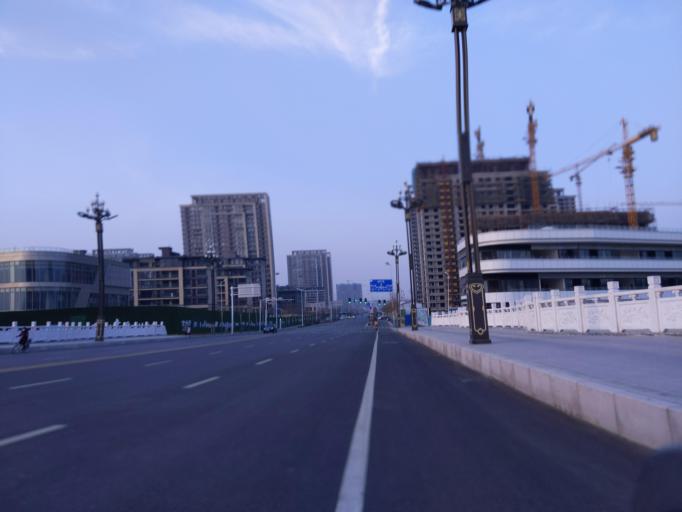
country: CN
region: Henan Sheng
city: Puyang
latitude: 35.8027
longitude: 115.0110
